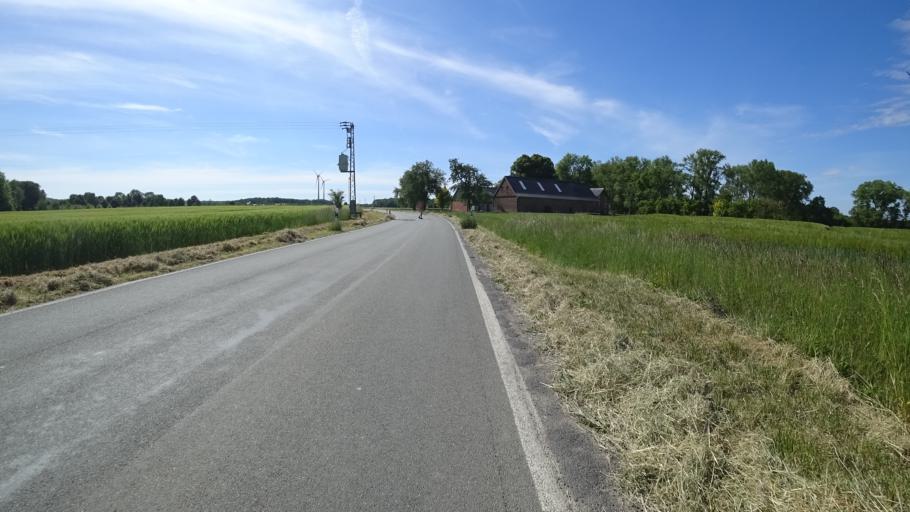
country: DE
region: North Rhine-Westphalia
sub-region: Regierungsbezirk Detmold
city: Rheda-Wiedenbruck
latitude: 51.8242
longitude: 8.2403
